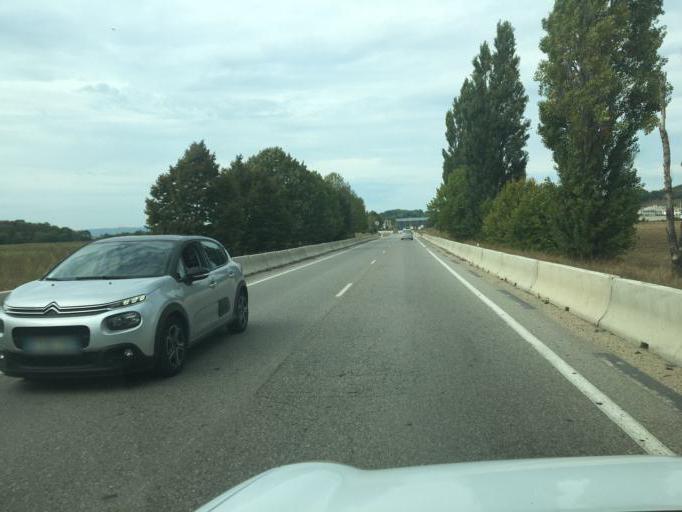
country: FR
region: Provence-Alpes-Cote d'Azur
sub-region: Departement des Bouches-du-Rhone
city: Bouc-Bel-Air
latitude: 43.4753
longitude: 5.3981
